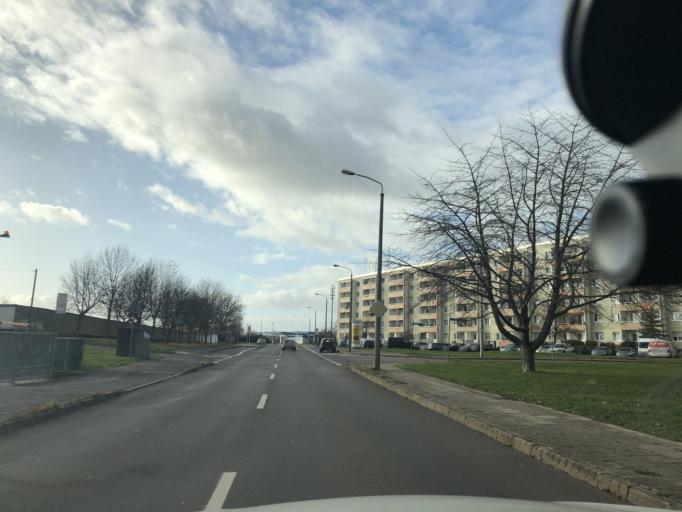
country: DE
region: Saxony-Anhalt
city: Halle Neustadt
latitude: 51.4726
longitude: 11.9088
